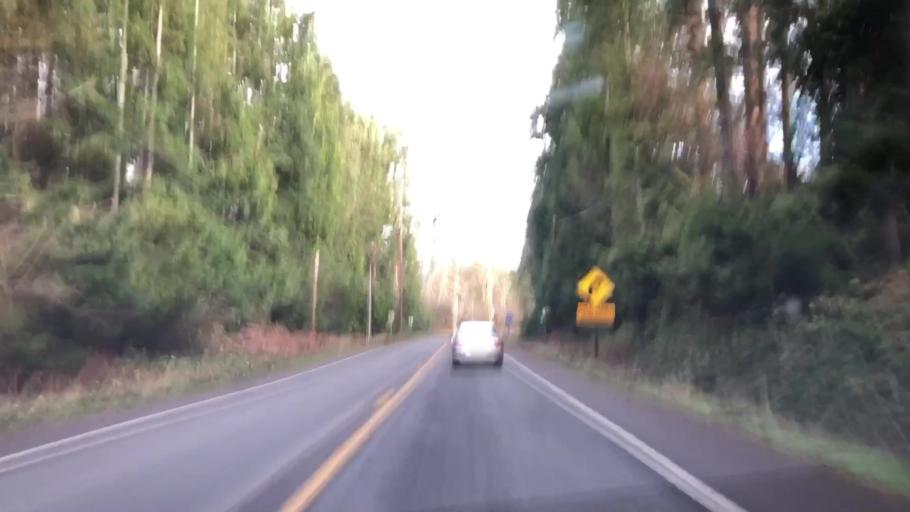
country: US
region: Washington
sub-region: Kitsap County
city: Suquamish
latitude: 47.7202
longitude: -122.5700
